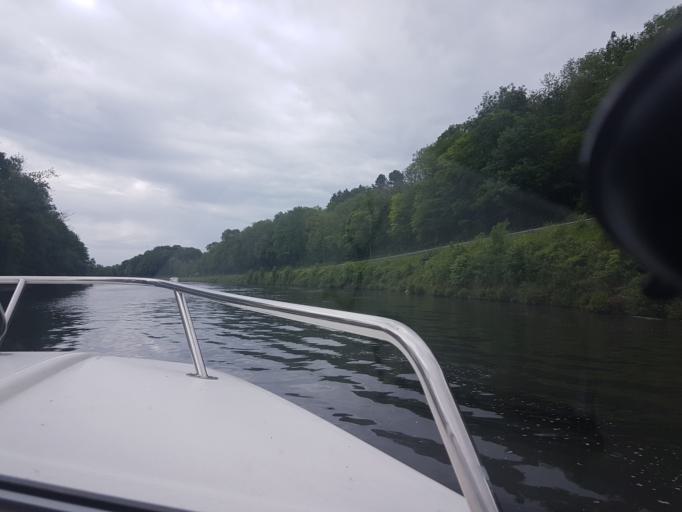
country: FR
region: Bourgogne
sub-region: Departement de l'Yonne
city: Champs-sur-Yonne
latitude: 47.7458
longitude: 3.5867
